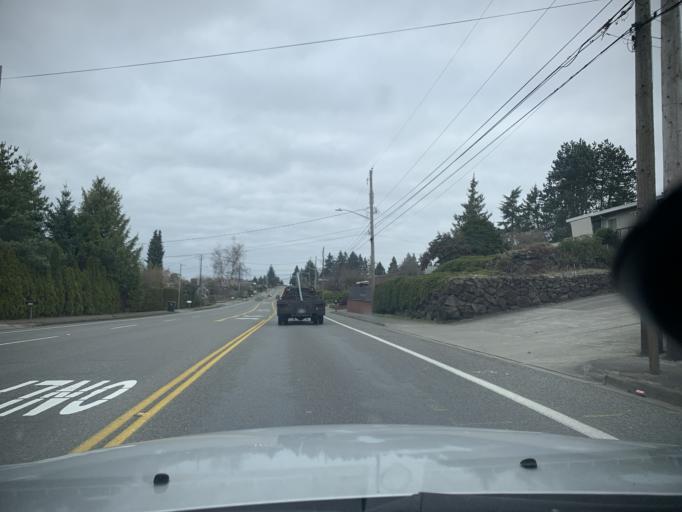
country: US
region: Washington
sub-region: Pierce County
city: University Place
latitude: 47.2602
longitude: -122.5371
